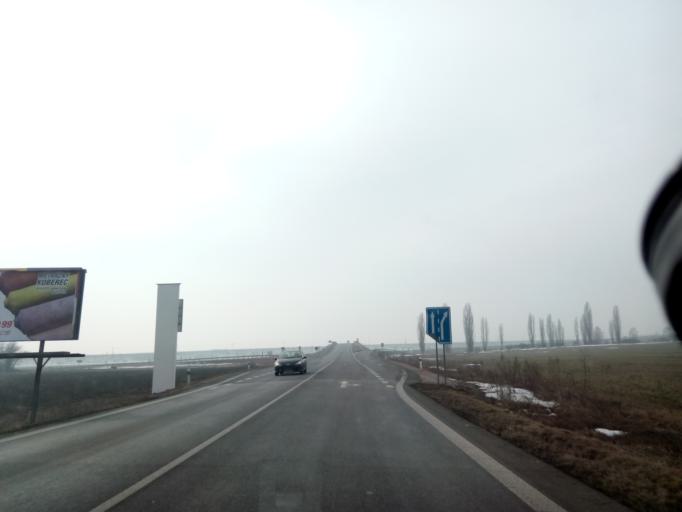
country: SK
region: Kosicky
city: Kosice
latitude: 48.6469
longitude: 21.2691
